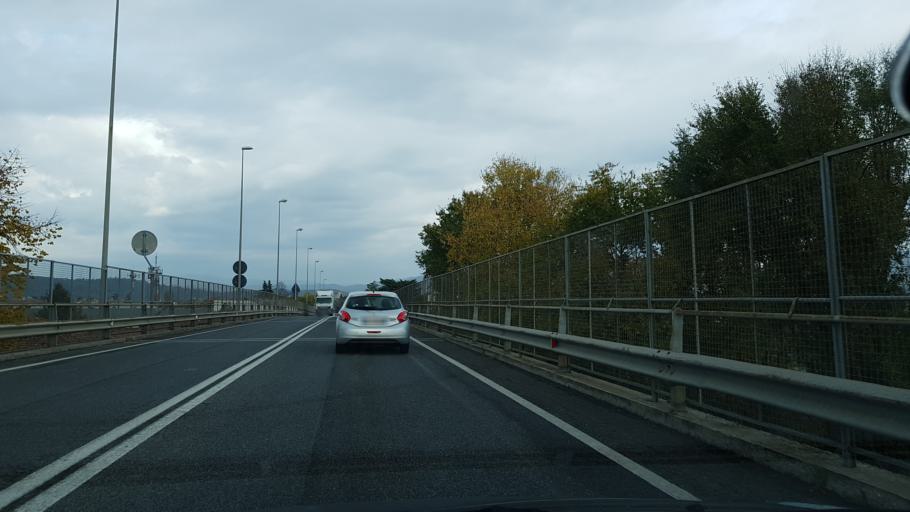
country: SI
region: Sempeter-Vrtojba
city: Vrtojba
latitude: 45.9199
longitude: 13.6136
